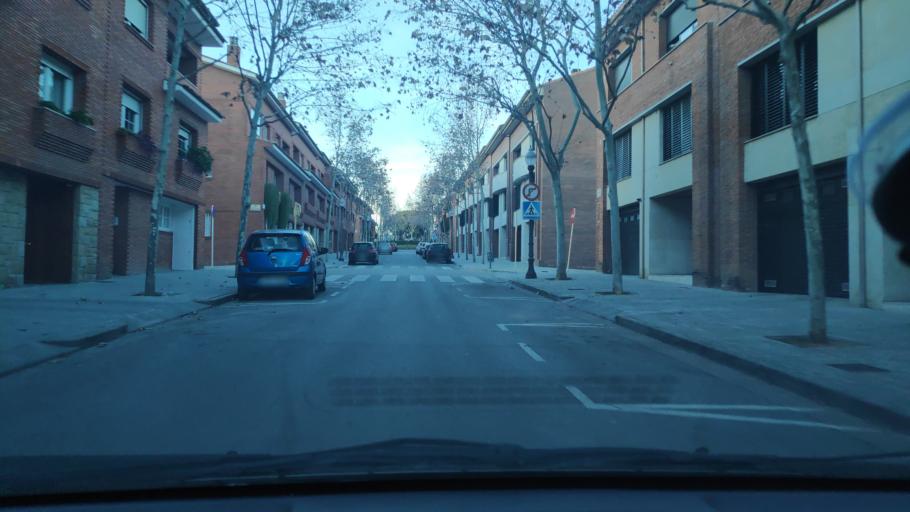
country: ES
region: Catalonia
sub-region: Provincia de Barcelona
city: Sant Quirze del Valles
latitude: 41.5336
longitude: 2.0841
